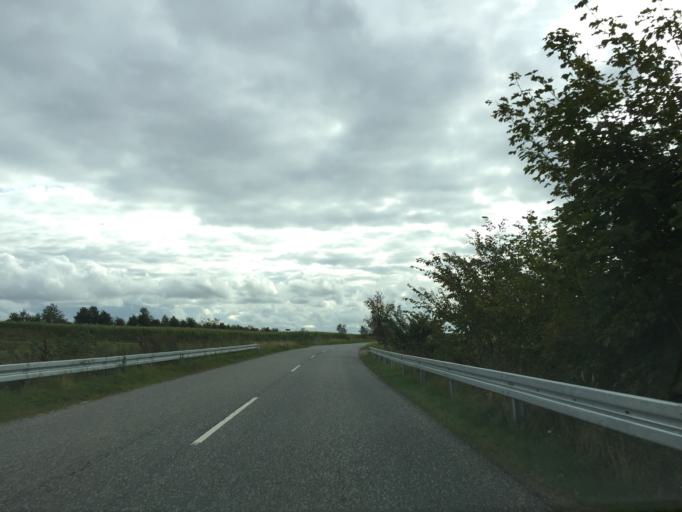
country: DK
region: Central Jutland
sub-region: Favrskov Kommune
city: Hammel
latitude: 56.2373
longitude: 9.7520
